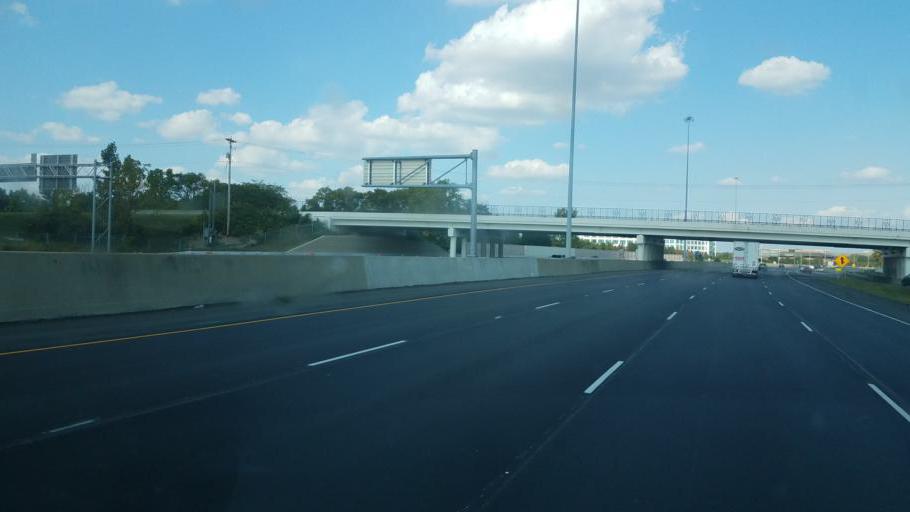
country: US
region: Ohio
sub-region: Franklin County
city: Dublin
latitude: 40.1013
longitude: -83.1321
